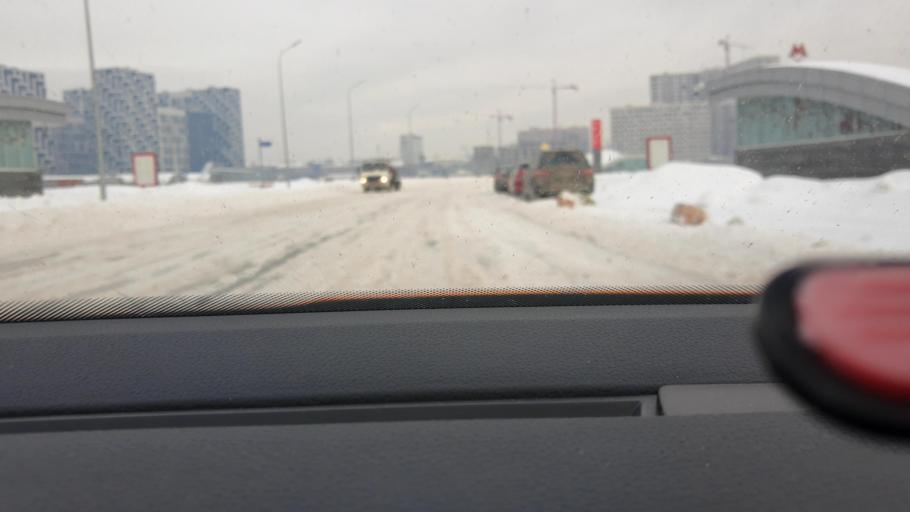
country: RU
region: Moscow
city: Strogino
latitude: 55.8173
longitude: 37.4347
